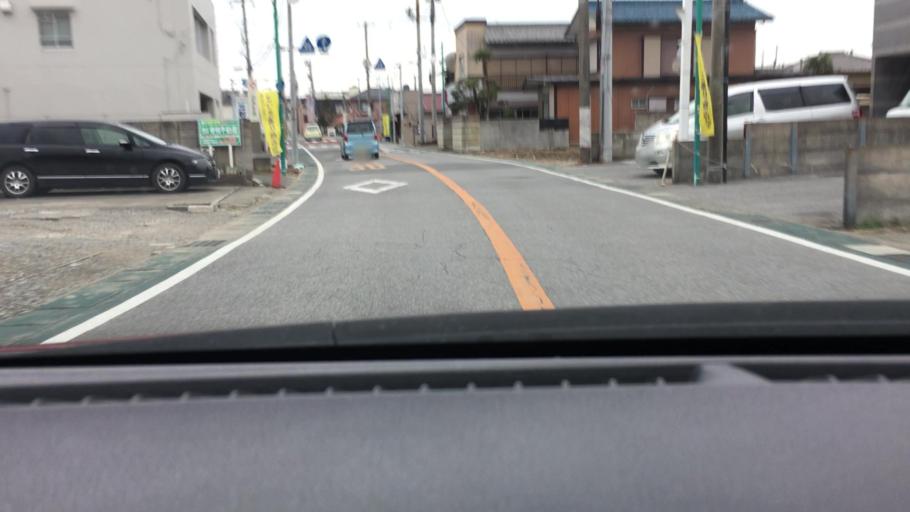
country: JP
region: Chiba
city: Kisarazu
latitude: 35.3840
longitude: 139.9277
